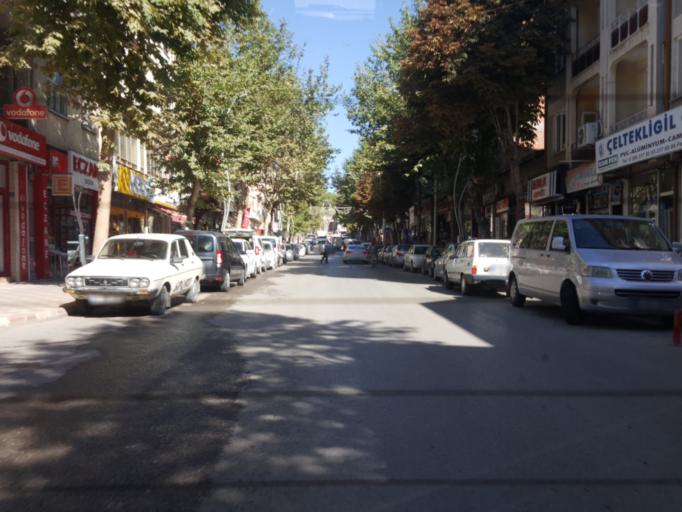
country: TR
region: Tokat
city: Zile
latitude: 40.3001
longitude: 35.8870
